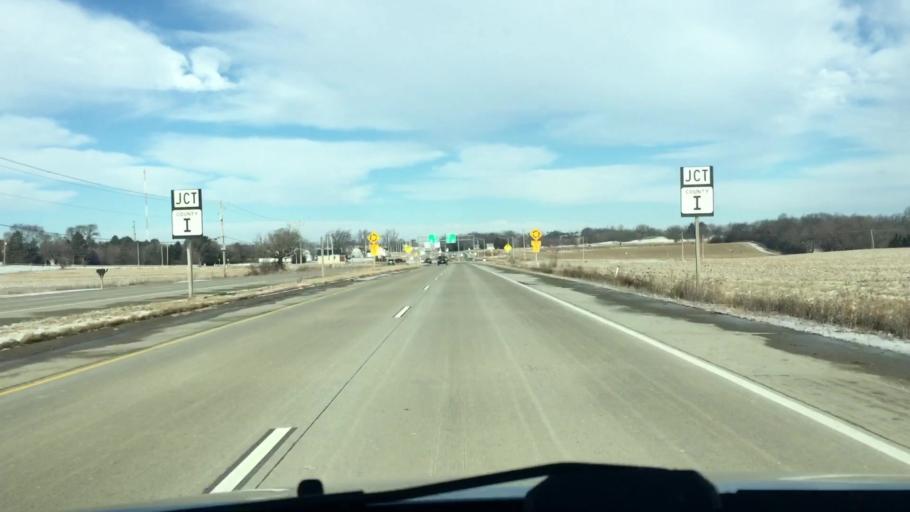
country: US
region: Wisconsin
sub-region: Waukesha County
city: Mukwonago
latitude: 42.9193
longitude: -88.3456
